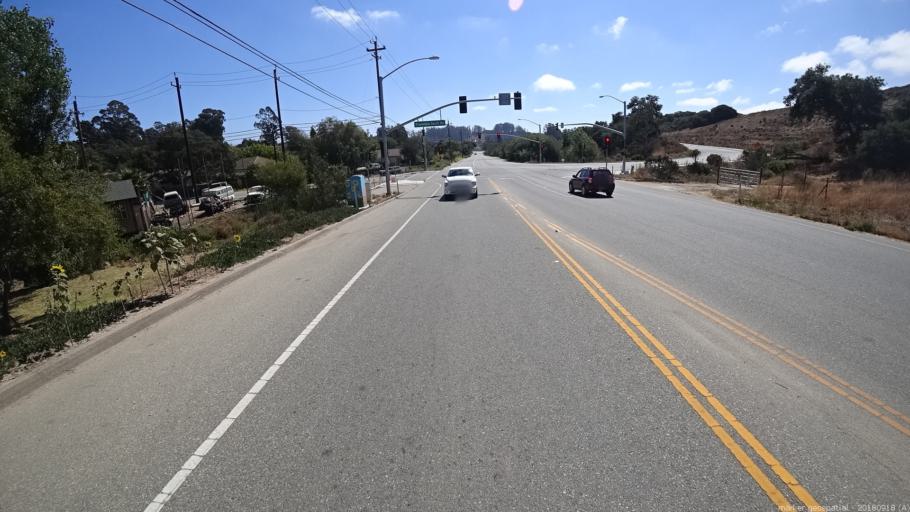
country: US
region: California
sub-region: Monterey County
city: Prunedale
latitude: 36.7749
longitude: -121.6723
